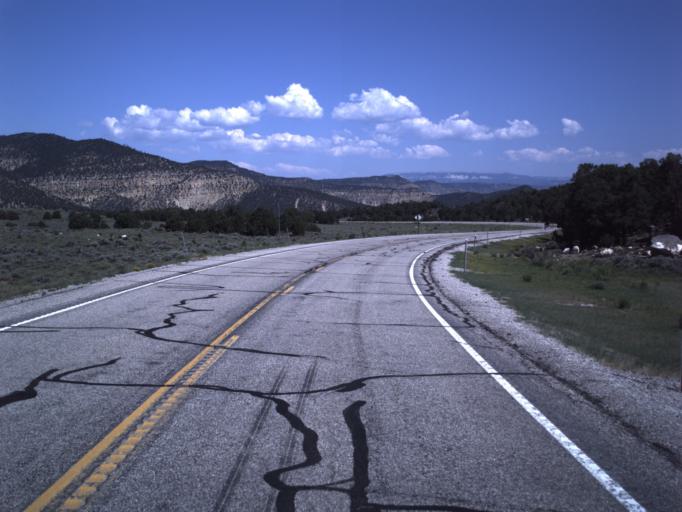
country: US
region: Utah
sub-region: Wayne County
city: Loa
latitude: 38.6945
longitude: -111.3965
